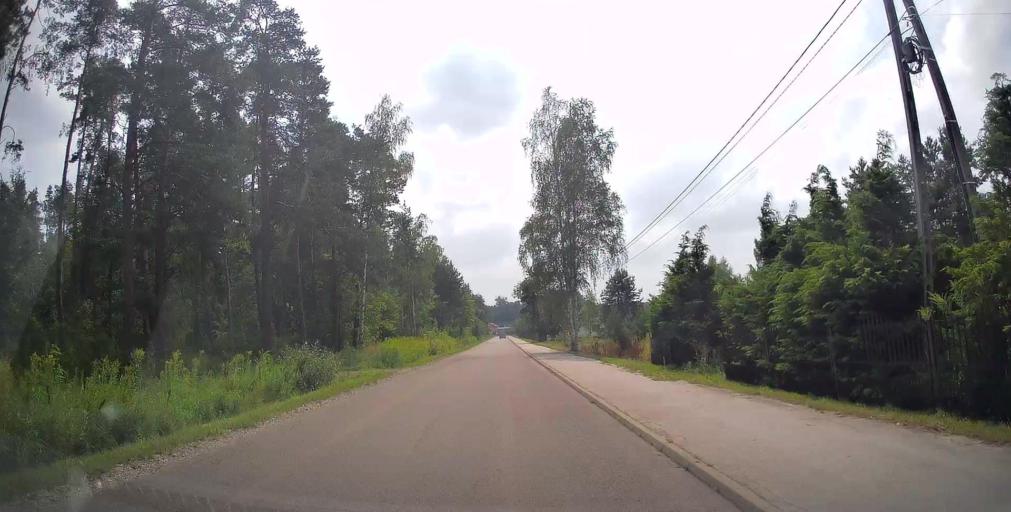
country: PL
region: Masovian Voivodeship
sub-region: Powiat bialobrzeski
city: Sucha
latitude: 51.6260
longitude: 20.9533
